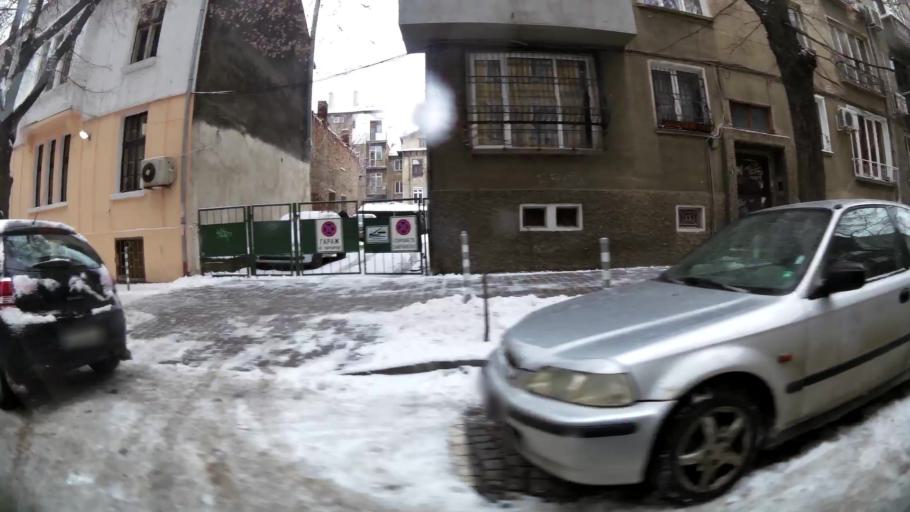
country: BG
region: Sofia-Capital
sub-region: Stolichna Obshtina
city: Sofia
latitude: 42.6959
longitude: 23.3400
